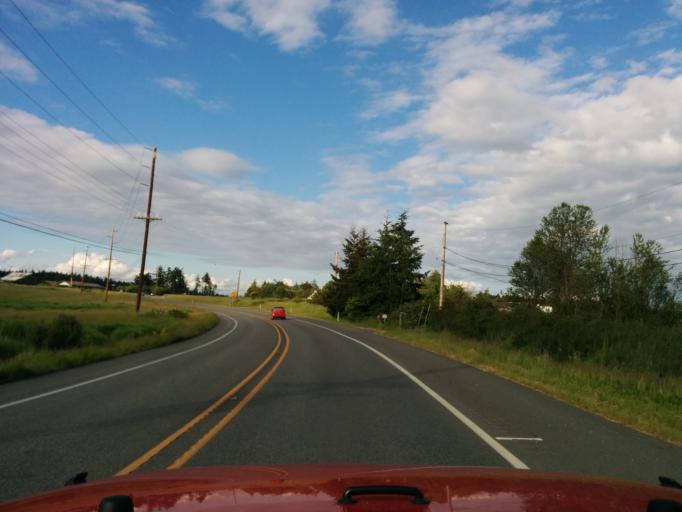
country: US
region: Washington
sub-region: Island County
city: Coupeville
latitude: 48.2572
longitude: -122.7017
